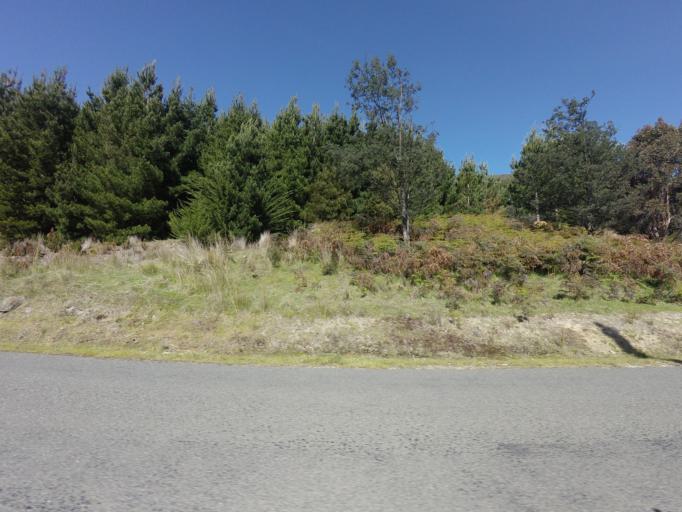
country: AU
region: Tasmania
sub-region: Derwent Valley
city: New Norfolk
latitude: -42.7421
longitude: 146.6575
